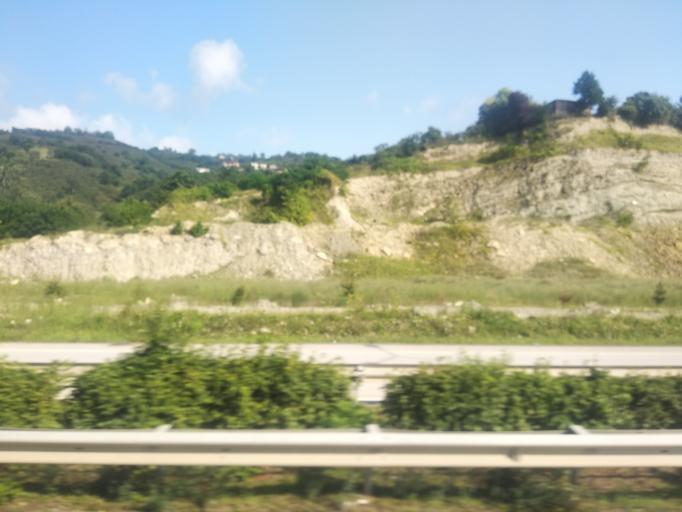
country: TR
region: Ordu
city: Ordu
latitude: 41.0018
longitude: 37.8242
